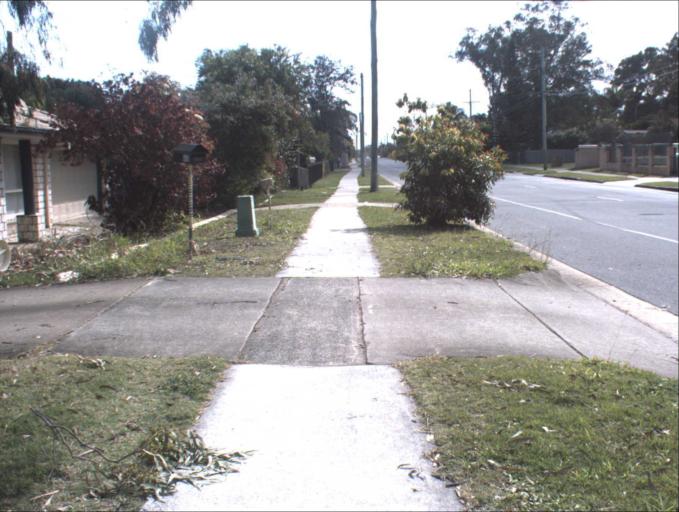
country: AU
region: Queensland
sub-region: Logan
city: Waterford West
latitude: -27.6780
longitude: 153.1004
